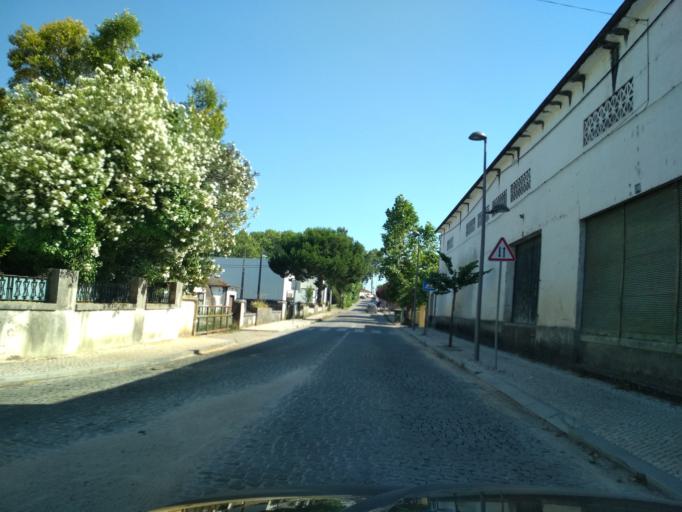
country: PT
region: Aveiro
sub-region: Mealhada
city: Mealhada
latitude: 40.3724
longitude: -8.4533
